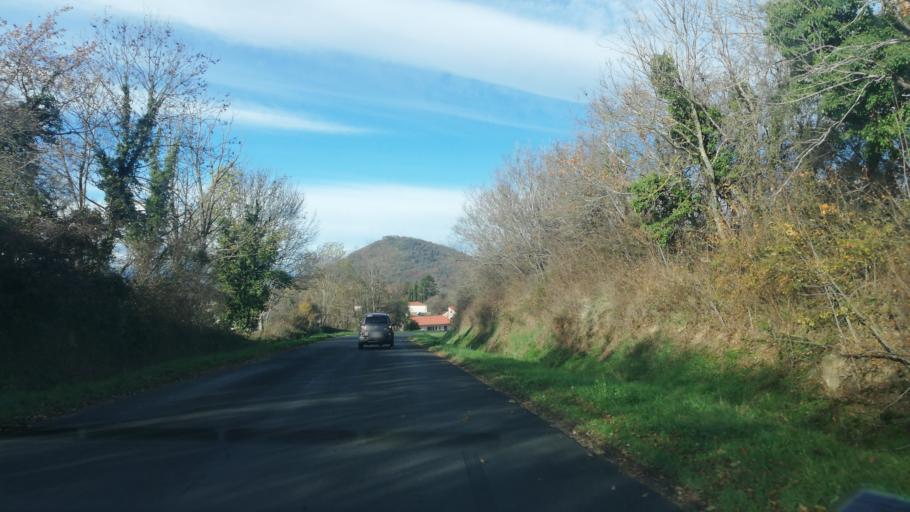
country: FR
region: Auvergne
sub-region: Departement du Puy-de-Dome
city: Billom
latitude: 45.7160
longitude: 3.3452
